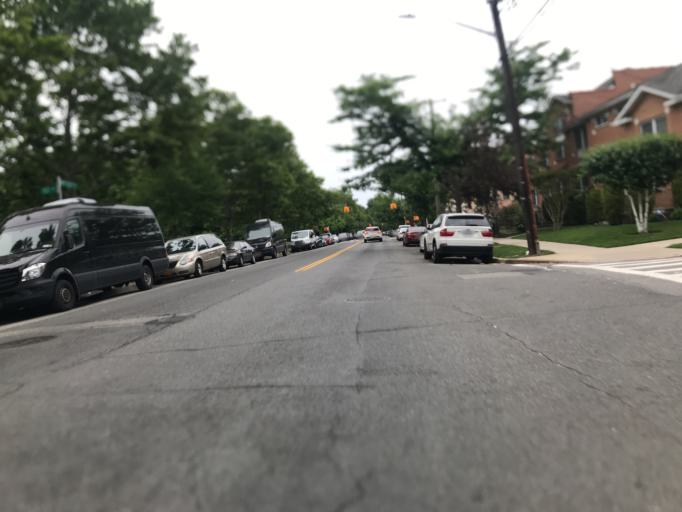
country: US
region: New York
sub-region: Queens County
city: Jamaica
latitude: 40.7425
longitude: -73.8114
